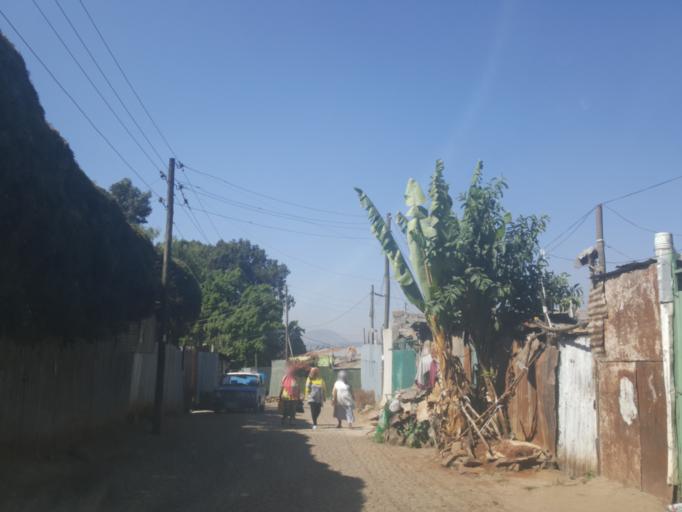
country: ET
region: Adis Abeba
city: Addis Ababa
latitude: 9.0614
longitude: 38.7249
